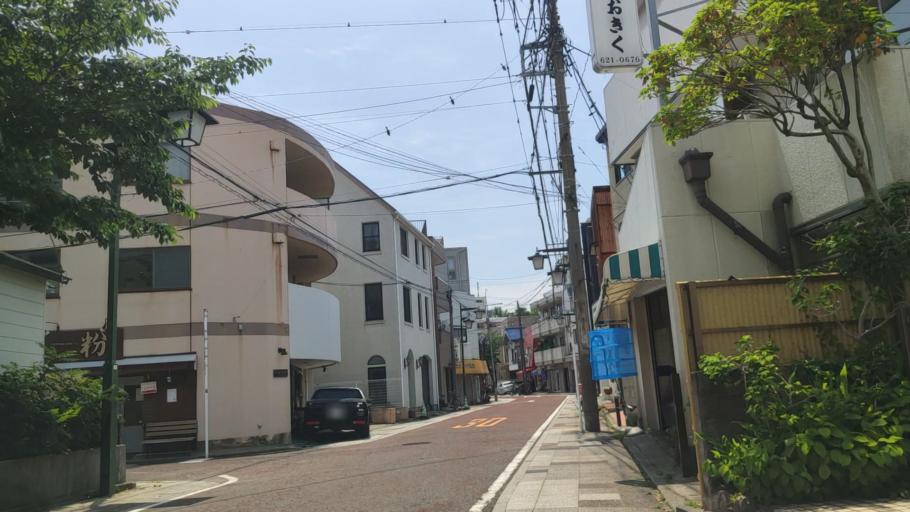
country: JP
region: Kanagawa
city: Yokohama
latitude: 35.4207
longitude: 139.6647
